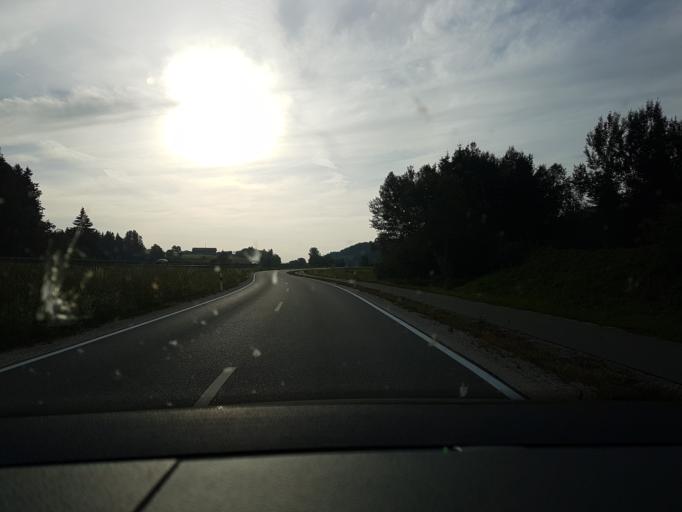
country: DE
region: Bavaria
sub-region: Upper Bavaria
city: Surberg
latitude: 47.8286
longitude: 12.7156
